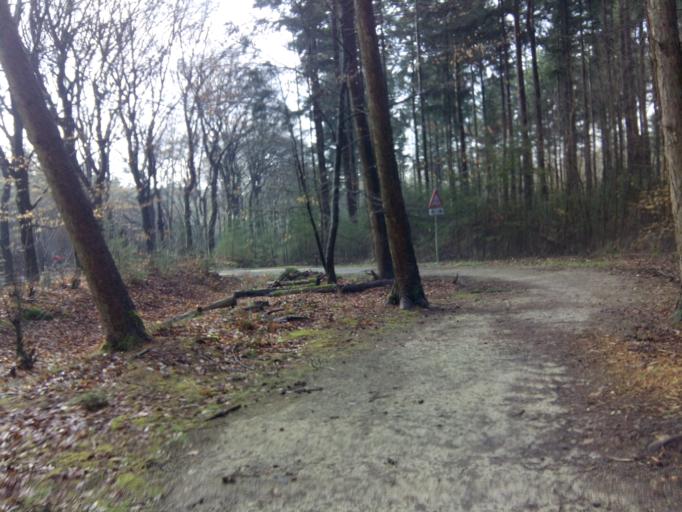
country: NL
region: Utrecht
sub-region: Gemeente Utrechtse Heuvelrug
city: Amerongen
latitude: 52.0101
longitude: 5.4532
